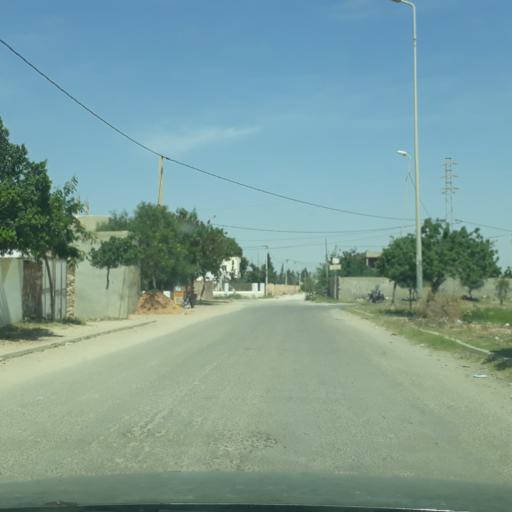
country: TN
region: Safaqis
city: Al Qarmadah
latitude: 34.8283
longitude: 10.7816
